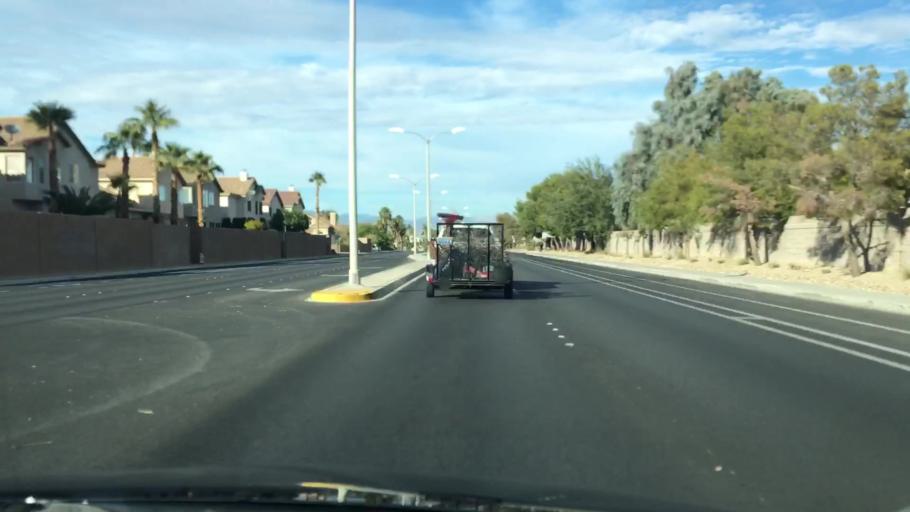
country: US
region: Nevada
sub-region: Clark County
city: Whitney
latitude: 36.0463
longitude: -115.1003
